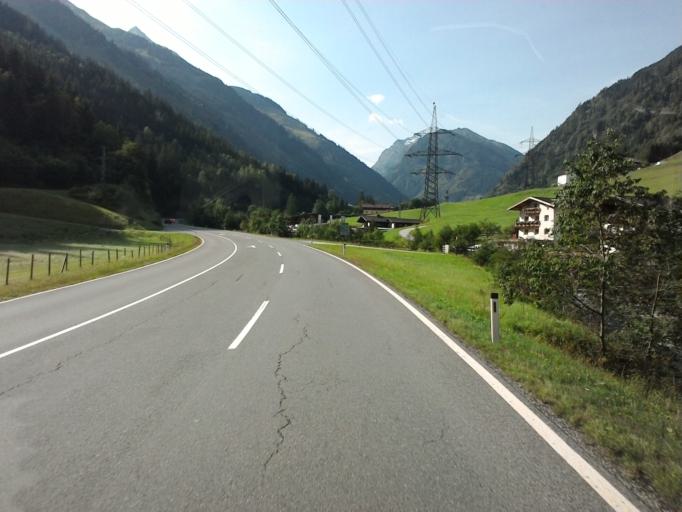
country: AT
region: Salzburg
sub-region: Politischer Bezirk Zell am See
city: Mittersill
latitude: 47.2529
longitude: 12.4861
